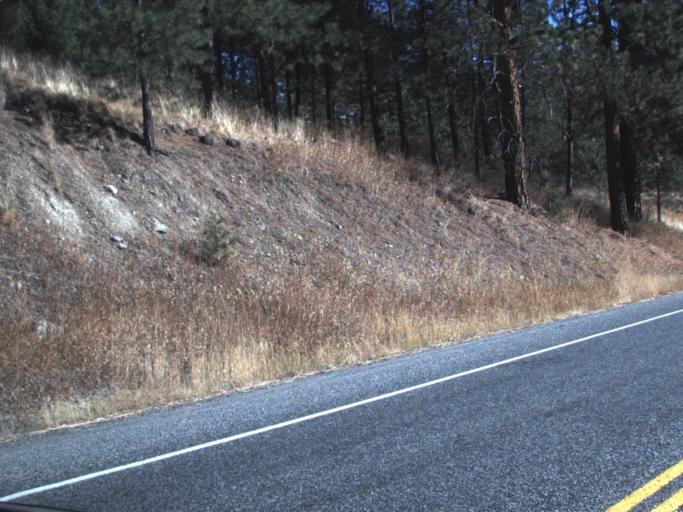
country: US
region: Washington
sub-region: Ferry County
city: Republic
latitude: 48.6489
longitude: -118.7529
